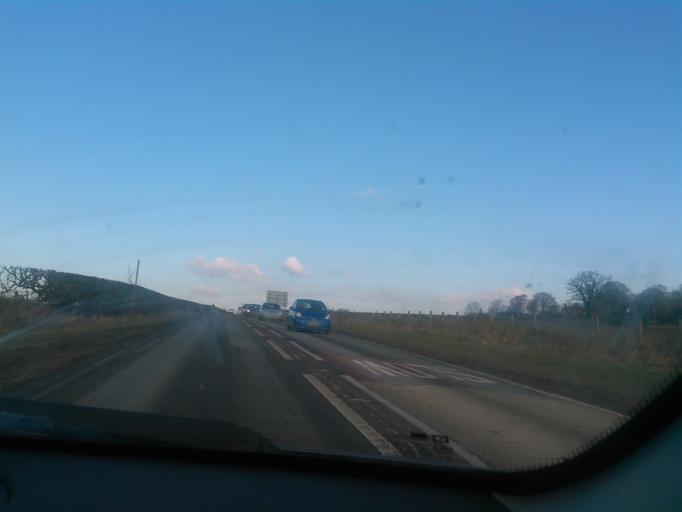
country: GB
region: England
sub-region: Shropshire
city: Clive
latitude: 52.8242
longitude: -2.6839
